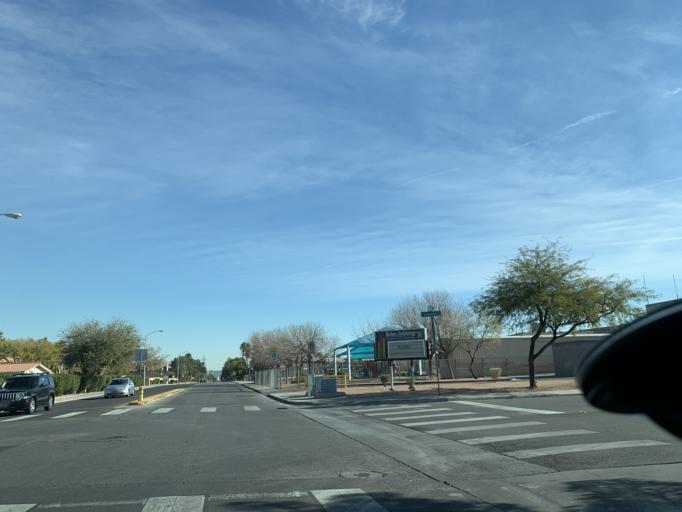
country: US
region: Nevada
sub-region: Clark County
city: Spring Valley
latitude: 36.0965
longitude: -115.2210
